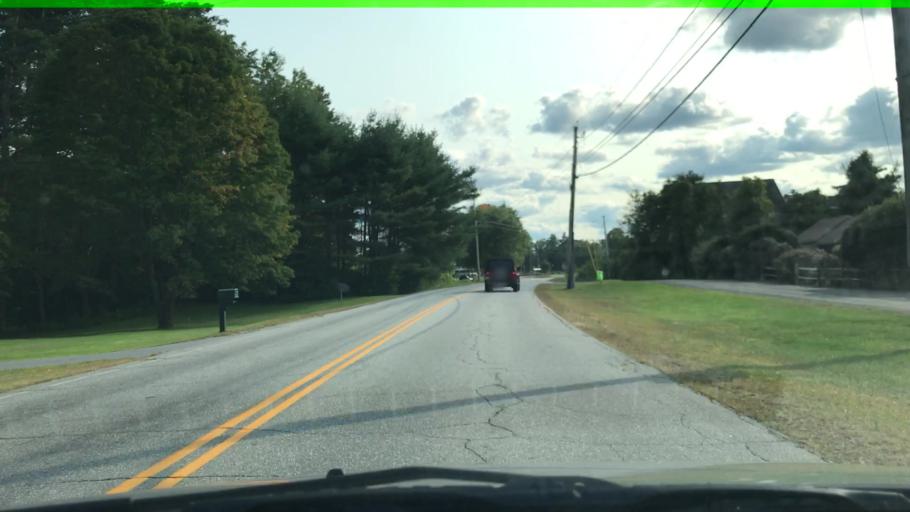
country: US
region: Vermont
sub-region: Windham County
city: Bellows Falls
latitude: 43.1070
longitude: -72.4238
